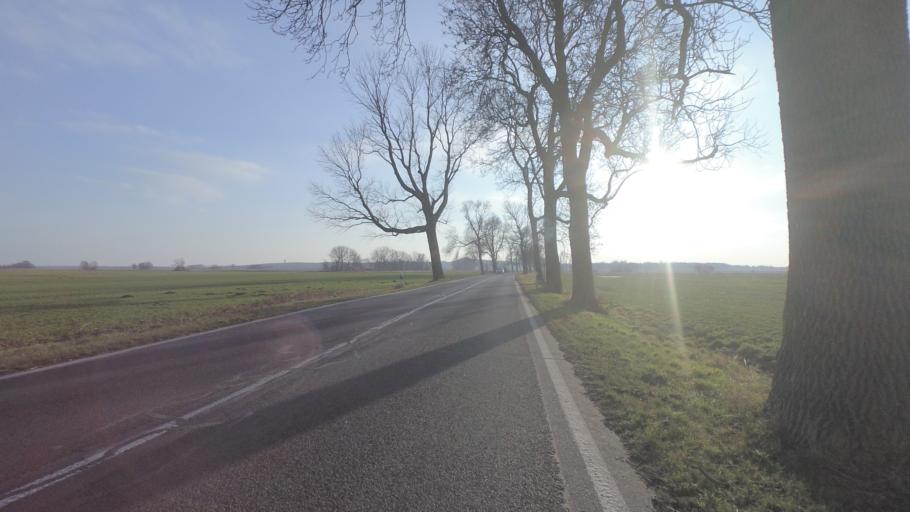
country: DE
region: Brandenburg
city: Rangsdorf
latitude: 52.2908
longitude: 13.3785
